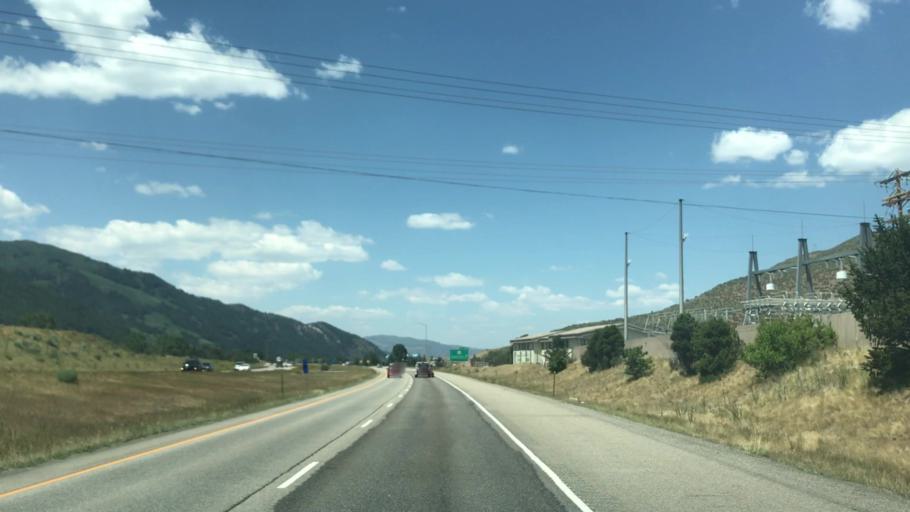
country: US
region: Colorado
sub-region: Eagle County
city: Avon
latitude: 39.6204
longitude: -106.4714
